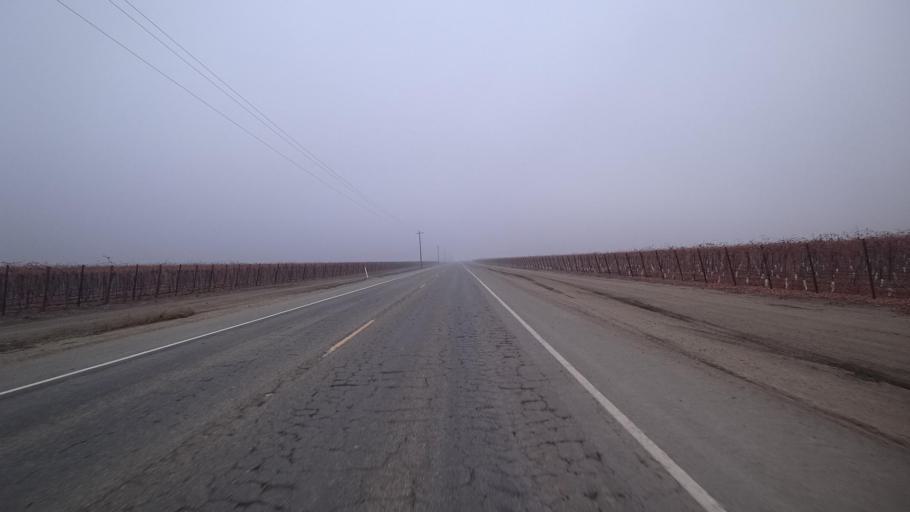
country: US
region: California
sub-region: Kern County
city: Buttonwillow
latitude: 35.4232
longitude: -119.5186
